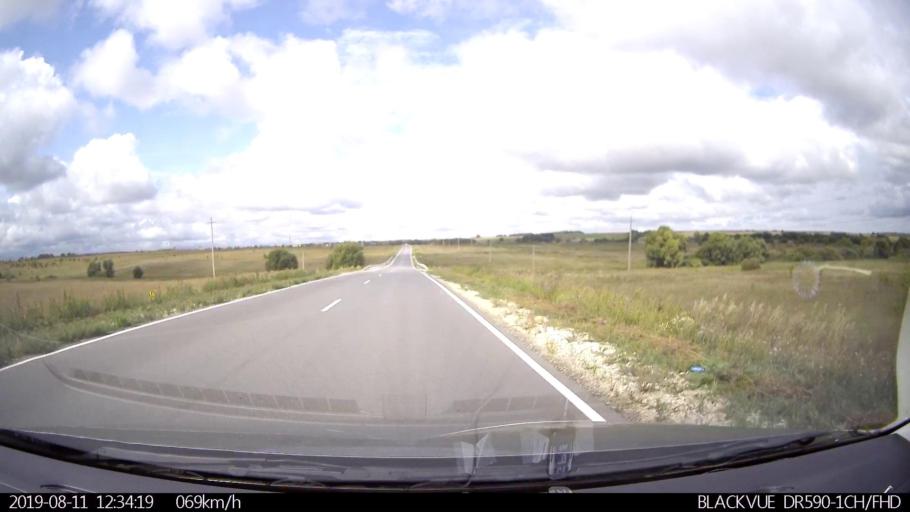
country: RU
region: Ulyanovsk
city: Ignatovka
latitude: 53.8158
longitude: 47.8448
